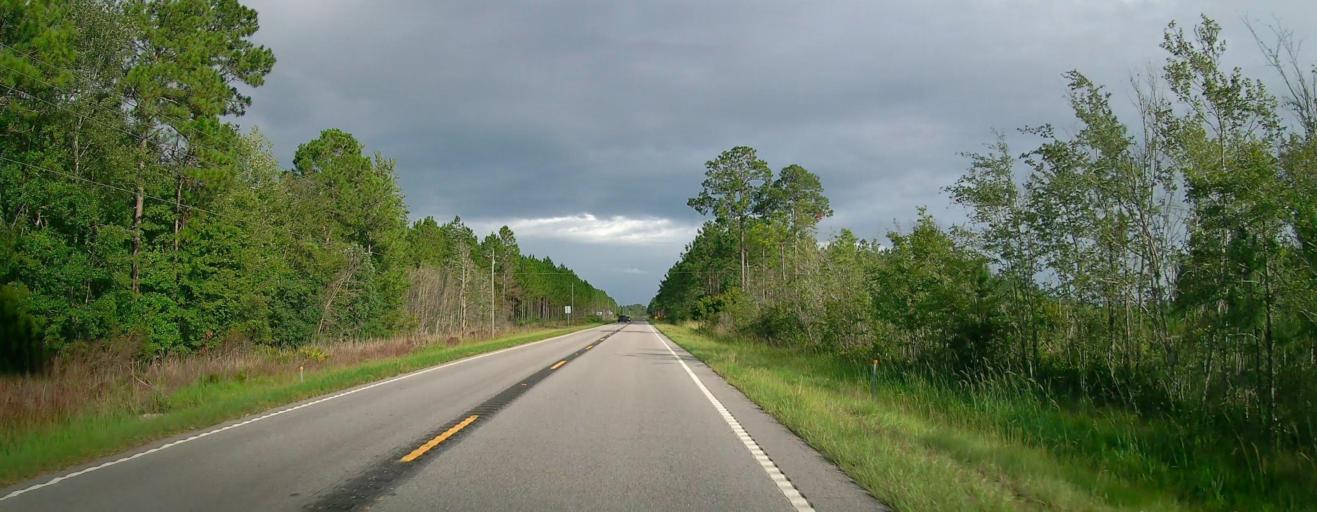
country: US
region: Georgia
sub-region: Coffee County
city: Nicholls
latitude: 31.3670
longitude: -82.6299
